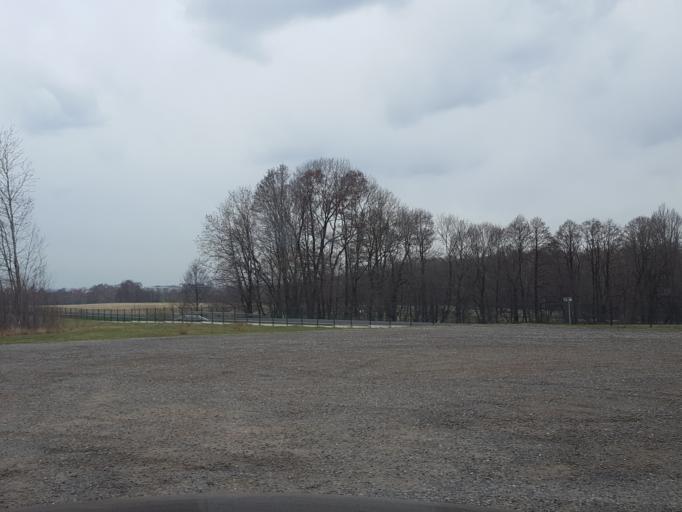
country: PL
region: Silesian Voivodeship
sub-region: Powiat mikolowski
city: Laziska Gorne
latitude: 50.1818
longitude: 18.8294
